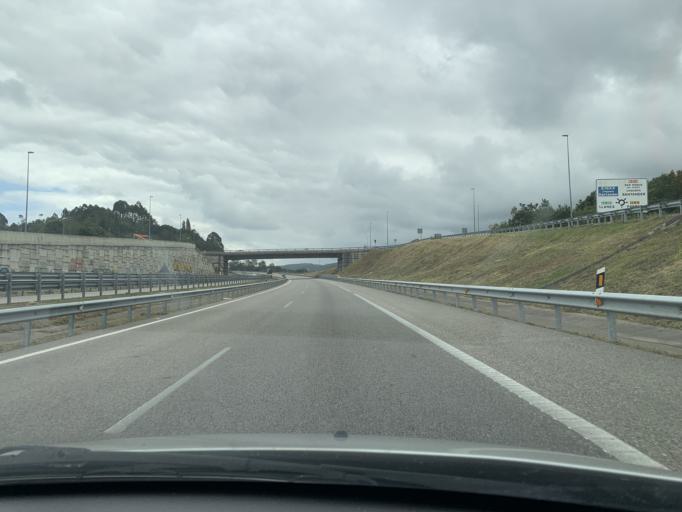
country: ES
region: Asturias
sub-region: Province of Asturias
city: Llanes
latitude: 43.4057
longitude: -4.7621
